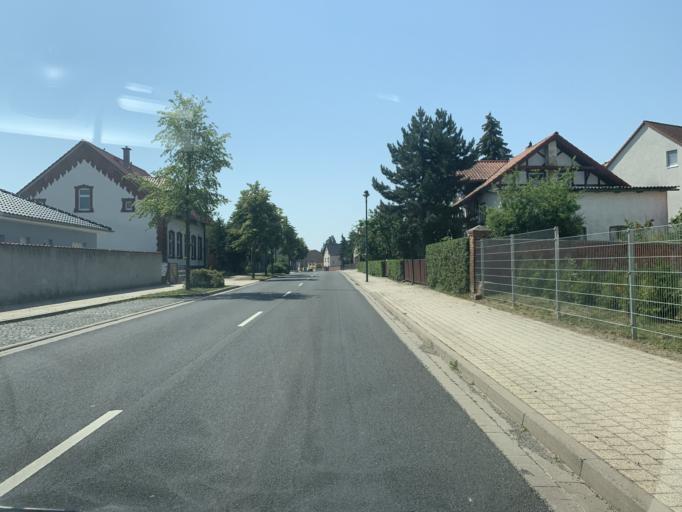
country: DE
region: Saxony-Anhalt
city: Erxleben
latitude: 52.2235
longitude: 11.2414
